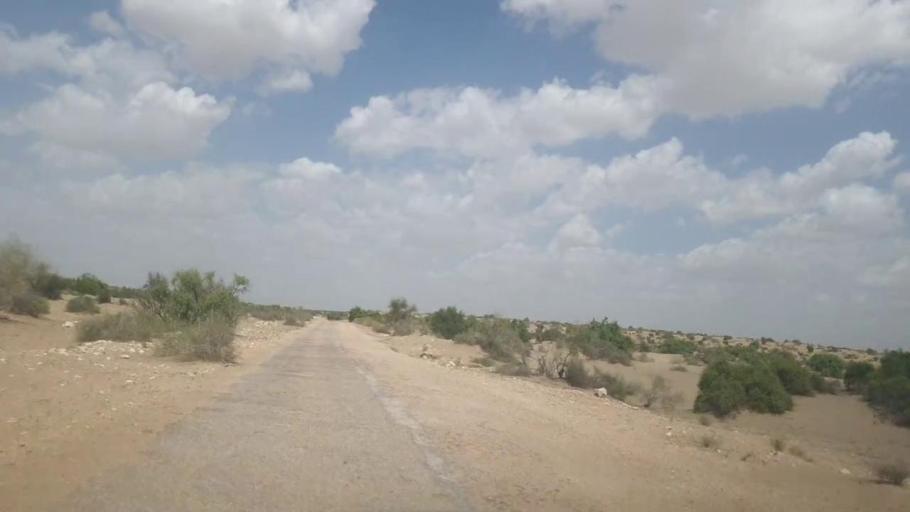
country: PK
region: Sindh
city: Kot Diji
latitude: 27.2694
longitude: 69.1898
